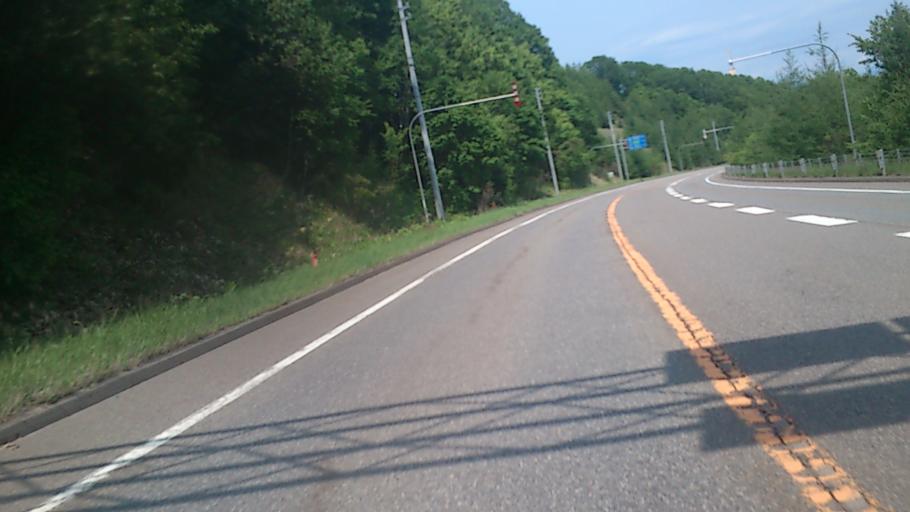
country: JP
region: Hokkaido
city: Otofuke
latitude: 43.2362
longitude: 143.5293
